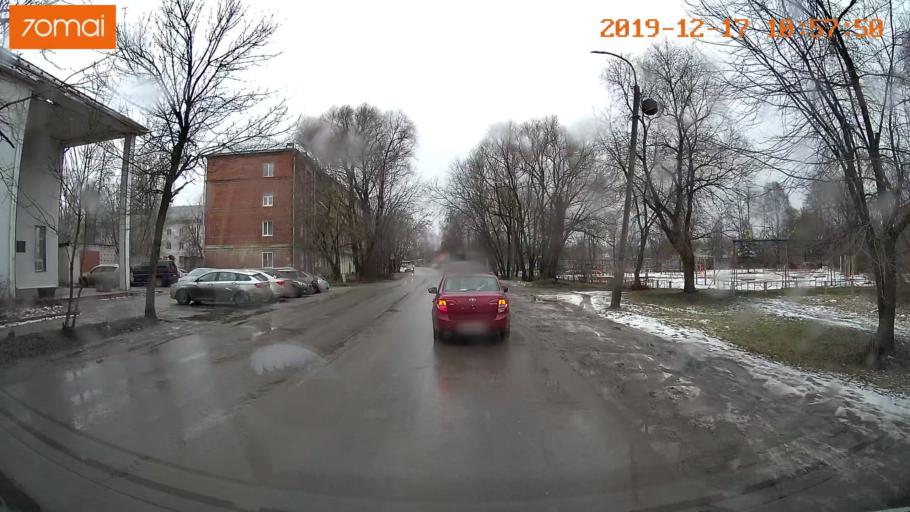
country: RU
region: Vladimir
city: Gus'-Khrustal'nyy
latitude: 55.6218
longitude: 40.6560
